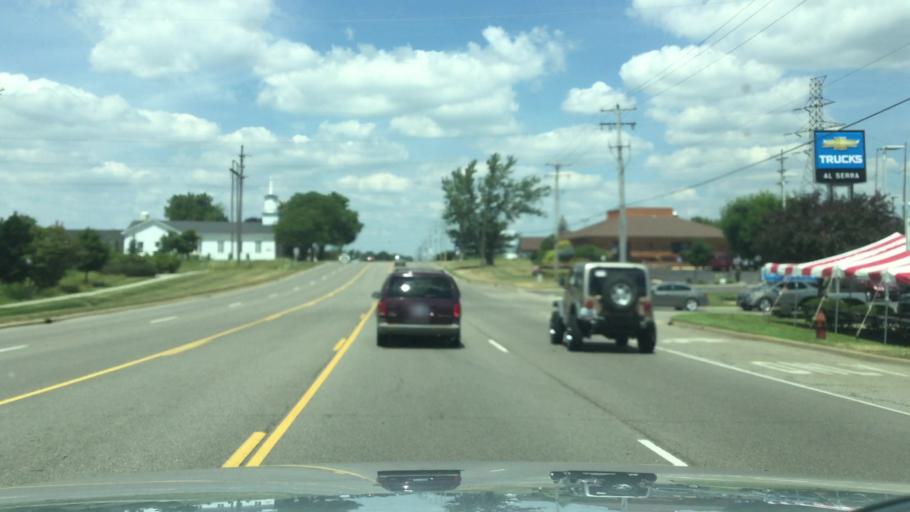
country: US
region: Michigan
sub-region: Genesee County
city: Grand Blanc
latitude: 42.9411
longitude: -83.6463
